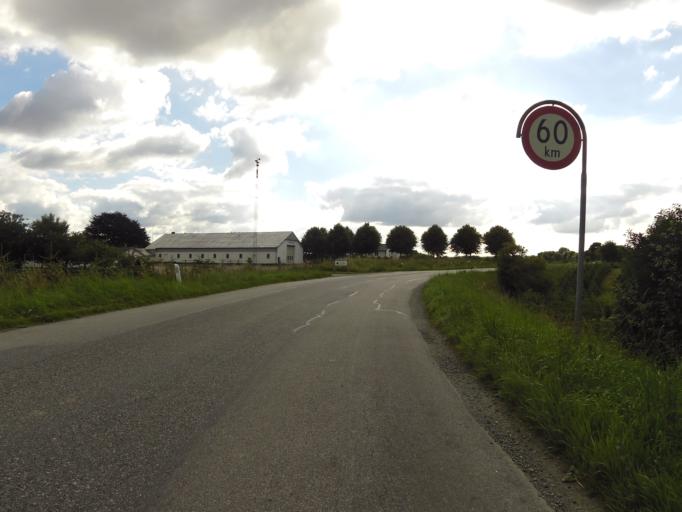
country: DK
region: South Denmark
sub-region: Haderslev Kommune
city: Haderslev
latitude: 55.2066
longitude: 9.4307
